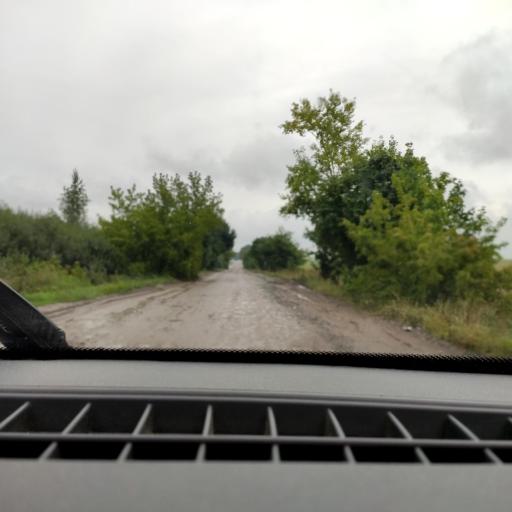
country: RU
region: Bashkortostan
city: Avdon
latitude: 54.7185
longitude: 55.7676
